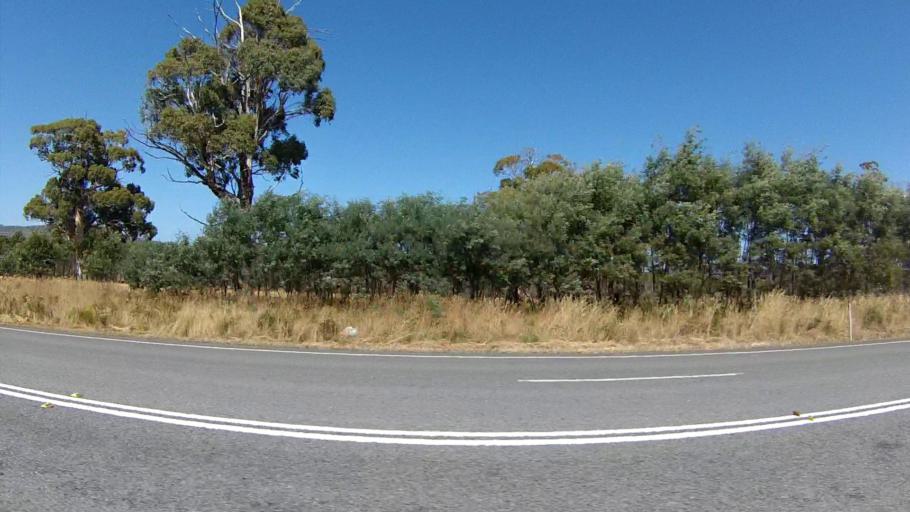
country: AU
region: Tasmania
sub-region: Sorell
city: Sorell
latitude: -42.6017
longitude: 147.7556
